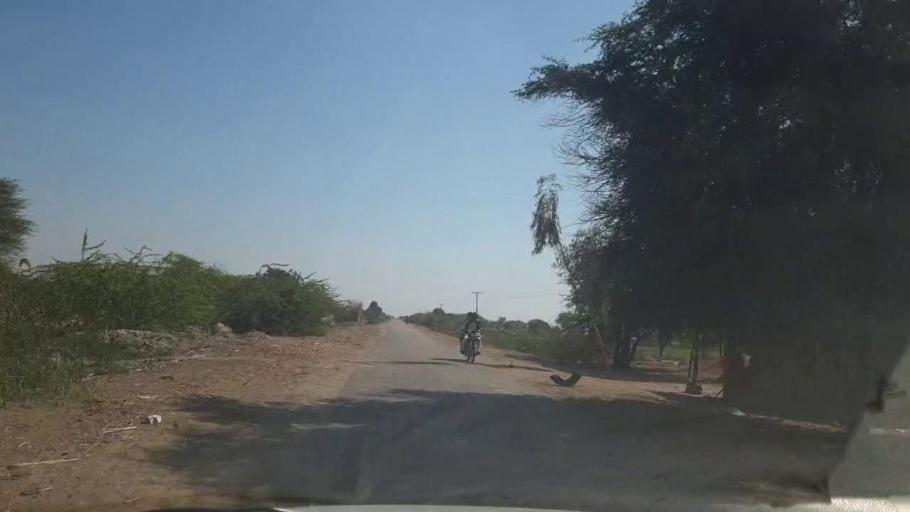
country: PK
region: Sindh
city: Mirpur Khas
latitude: 25.4751
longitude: 69.1745
